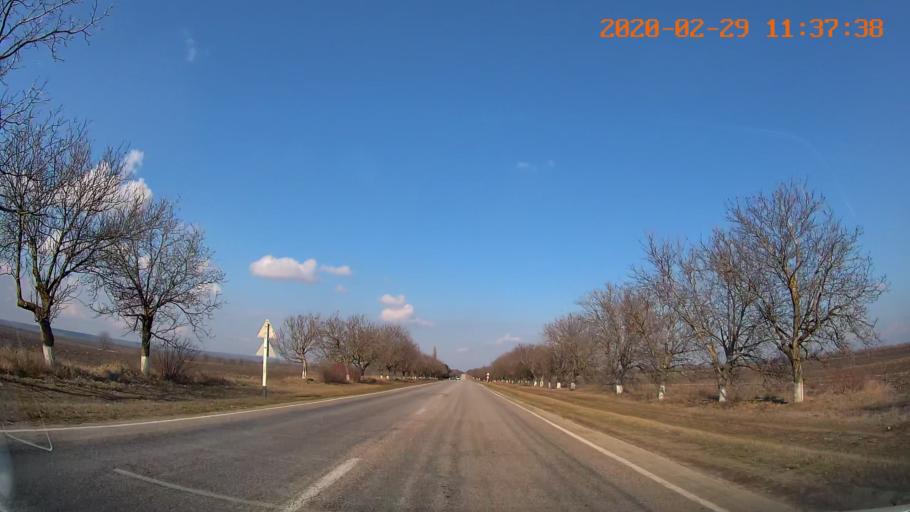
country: MD
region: Rezina
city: Saharna
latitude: 47.6144
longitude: 29.0443
